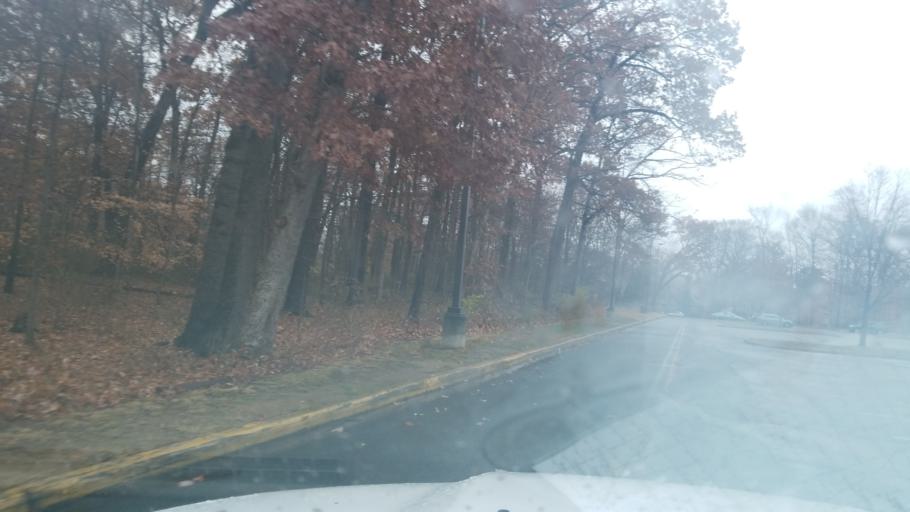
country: US
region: Maryland
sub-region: Montgomery County
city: Silver Spring
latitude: 38.9521
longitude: -77.0396
